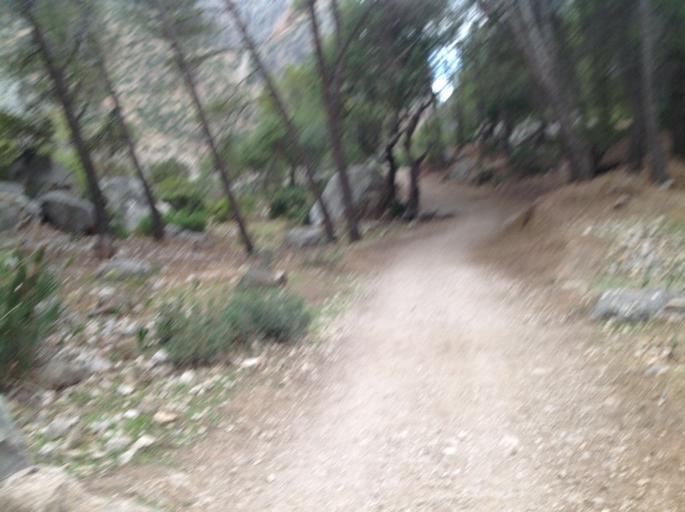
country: ES
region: Andalusia
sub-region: Provincia de Malaga
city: Ardales
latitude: 36.9225
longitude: -4.7811
